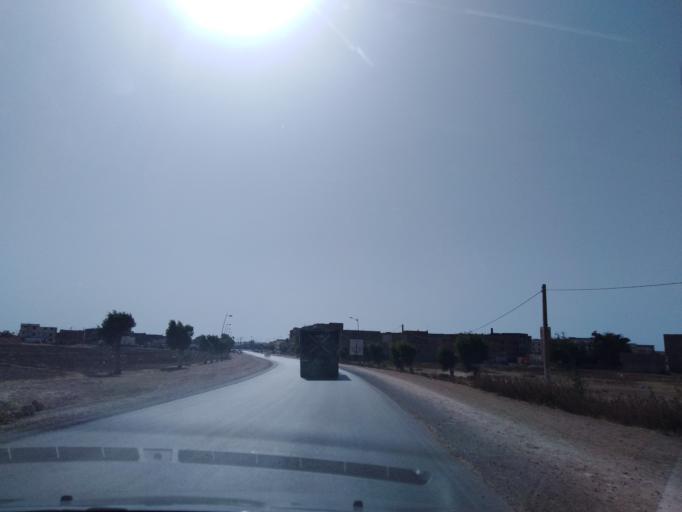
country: MA
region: Doukkala-Abda
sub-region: Safi
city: Safi
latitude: 32.2534
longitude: -8.9772
